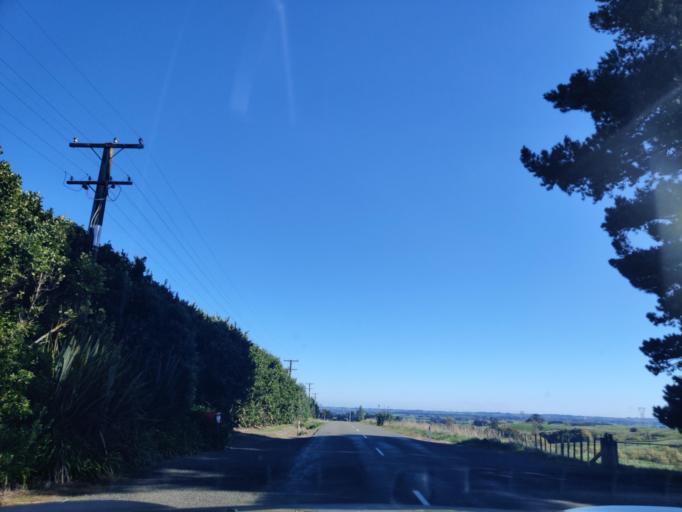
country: NZ
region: Manawatu-Wanganui
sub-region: Palmerston North City
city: Palmerston North
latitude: -40.2502
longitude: 175.6865
